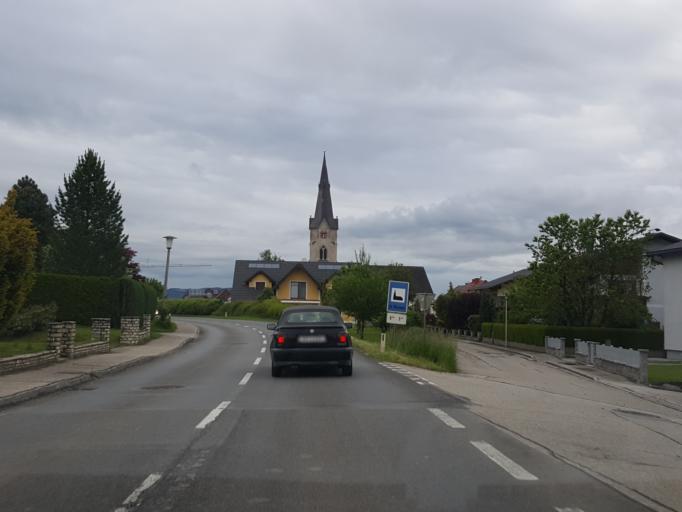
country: AT
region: Upper Austria
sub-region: Politischer Bezirk Vocklabruck
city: Gampern
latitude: 47.9864
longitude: 13.5551
